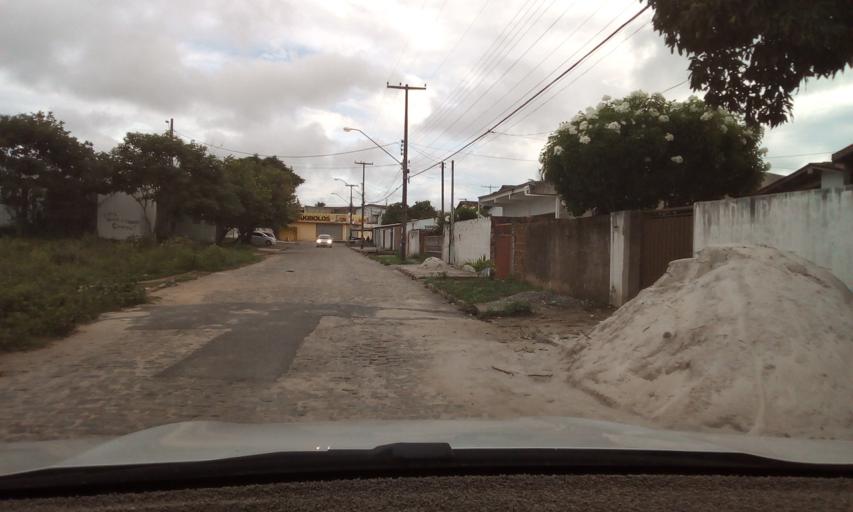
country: BR
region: Paraiba
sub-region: Joao Pessoa
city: Joao Pessoa
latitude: -7.1765
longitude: -34.8212
